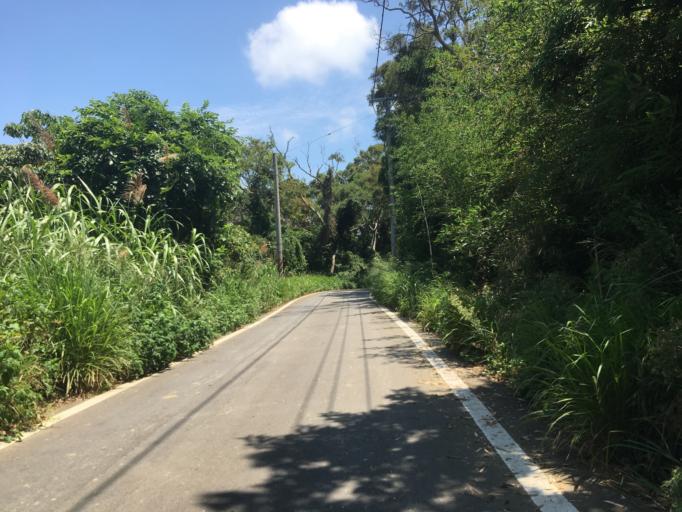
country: TW
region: Taiwan
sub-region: Hsinchu
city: Hsinchu
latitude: 24.7357
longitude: 120.9874
